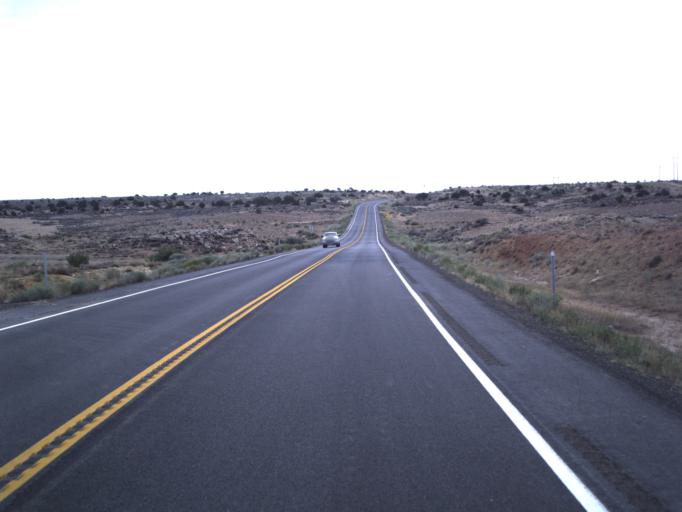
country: US
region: Utah
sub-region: Uintah County
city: Naples
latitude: 40.1973
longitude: -109.3353
